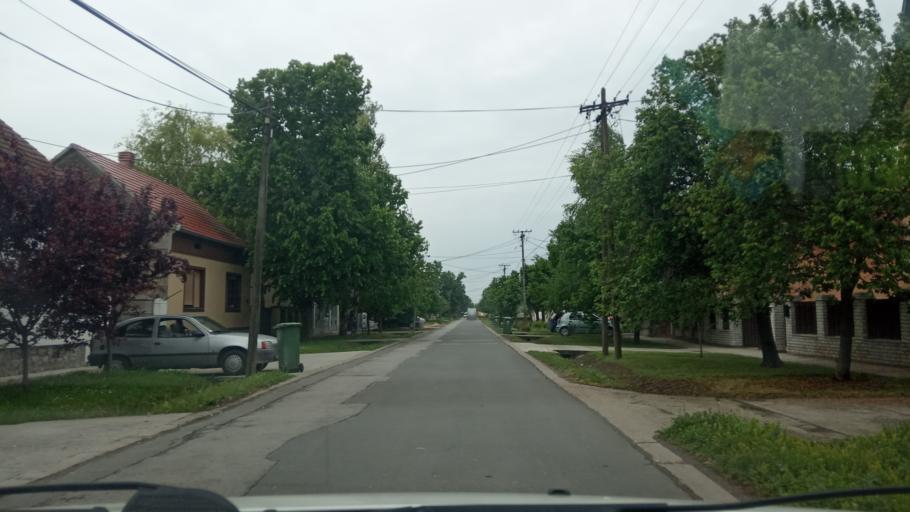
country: RS
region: Autonomna Pokrajina Vojvodina
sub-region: Sremski Okrug
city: Stara Pazova
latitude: 44.9936
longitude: 20.1525
